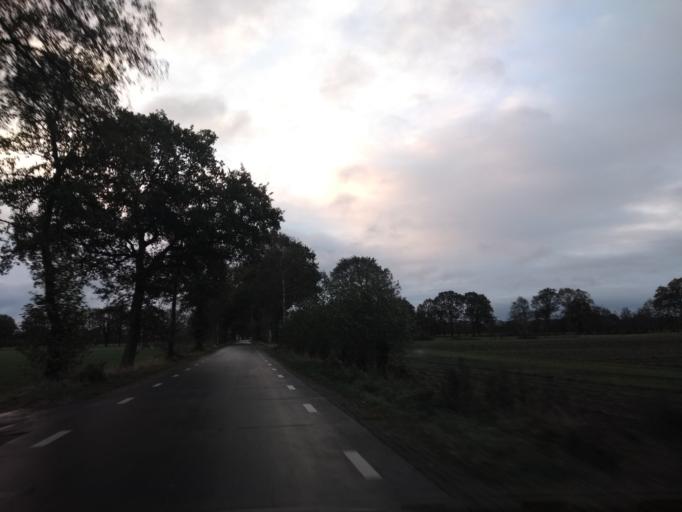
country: NL
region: Gelderland
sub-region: Gemeente Bronckhorst
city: Zelhem
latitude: 52.0257
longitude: 6.3603
